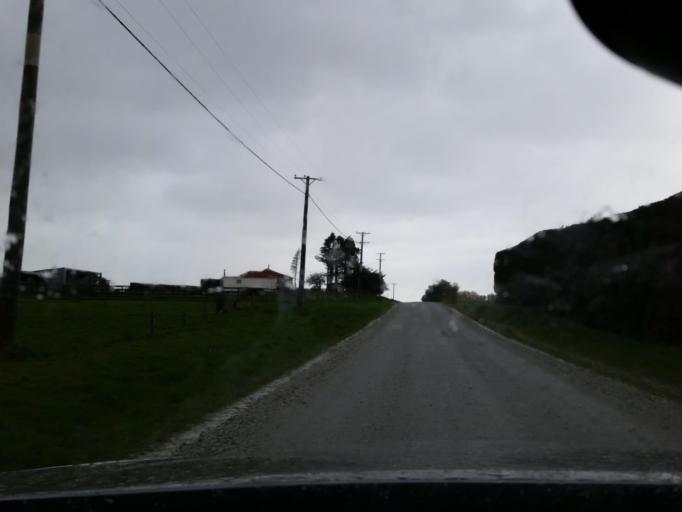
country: NZ
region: Southland
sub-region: Invercargill City
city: Invercargill
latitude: -46.4232
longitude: 168.5061
